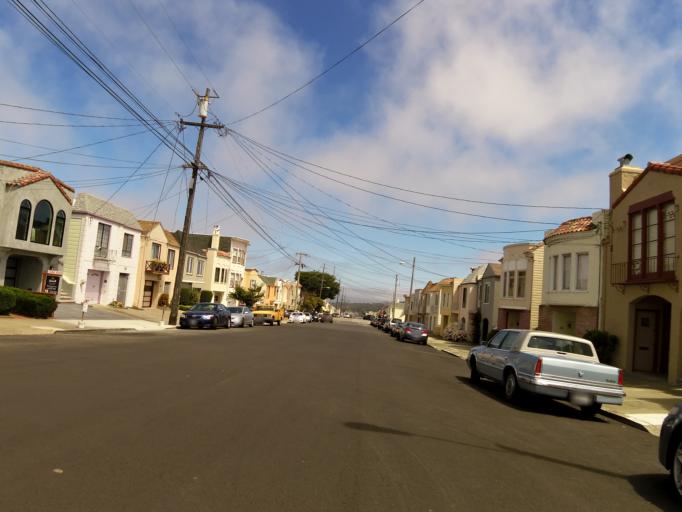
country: US
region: California
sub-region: San Mateo County
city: Daly City
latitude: 37.7492
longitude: -122.4772
